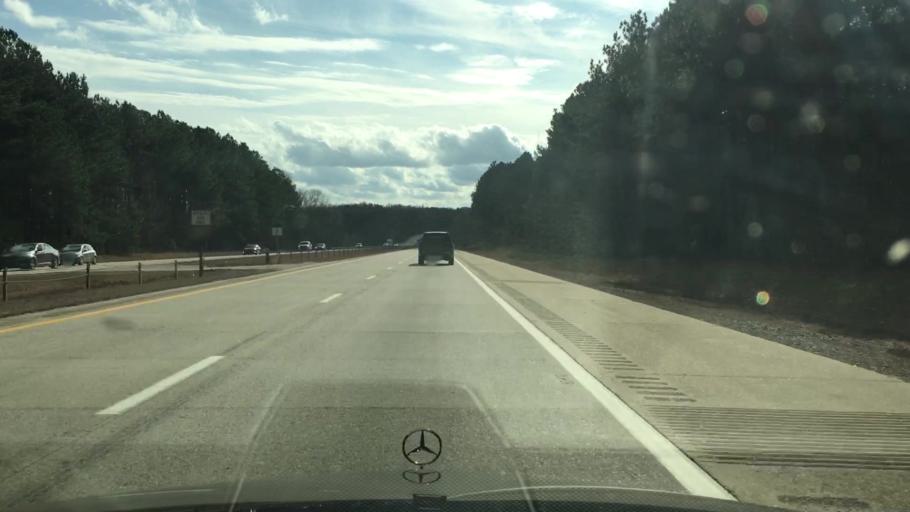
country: US
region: North Carolina
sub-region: Johnston County
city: Clayton
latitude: 35.5695
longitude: -78.5763
